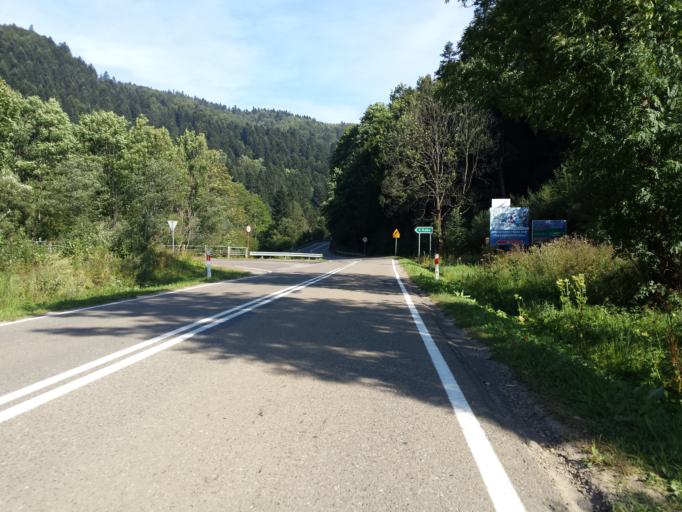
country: PL
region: Subcarpathian Voivodeship
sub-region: Powiat leski
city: Baligrod
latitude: 49.3156
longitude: 22.2752
